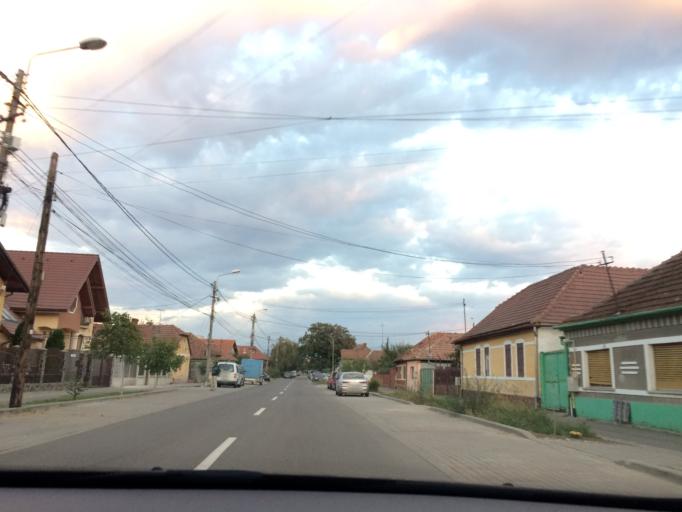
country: RO
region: Timis
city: Timisoara
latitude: 45.7610
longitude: 21.1961
